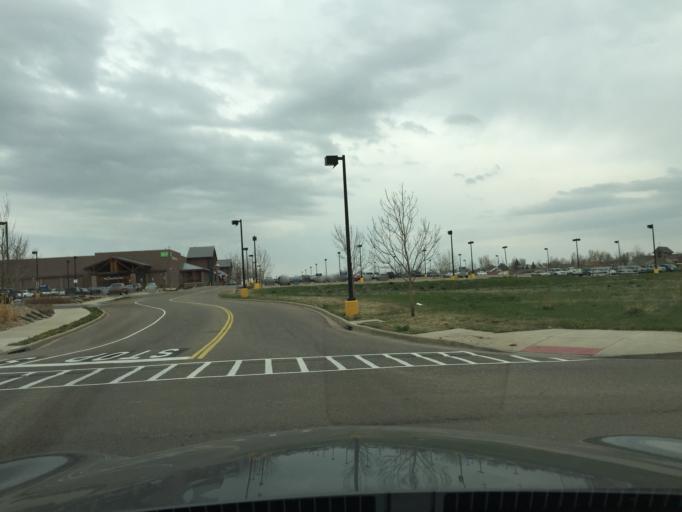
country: US
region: Colorado
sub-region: Boulder County
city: Lafayette
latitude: 40.0038
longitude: -105.1043
